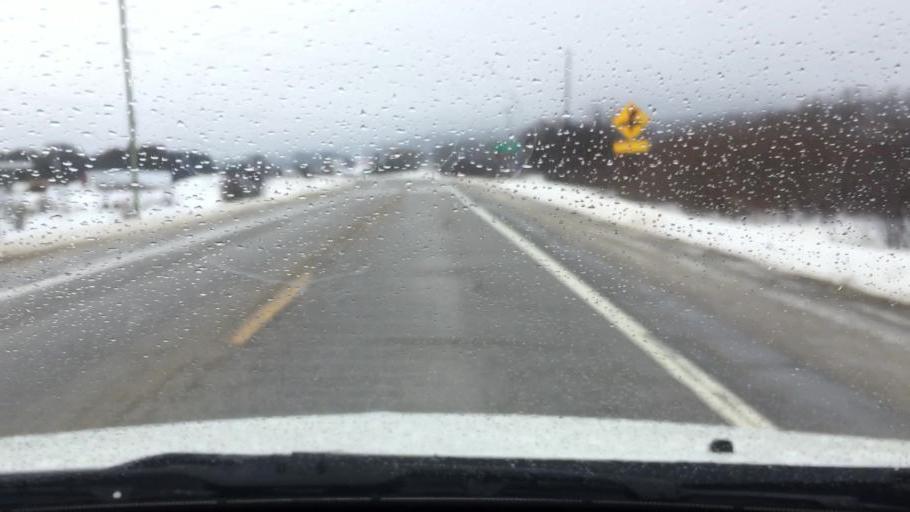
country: US
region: Michigan
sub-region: Charlevoix County
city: East Jordan
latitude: 45.1350
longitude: -85.1398
